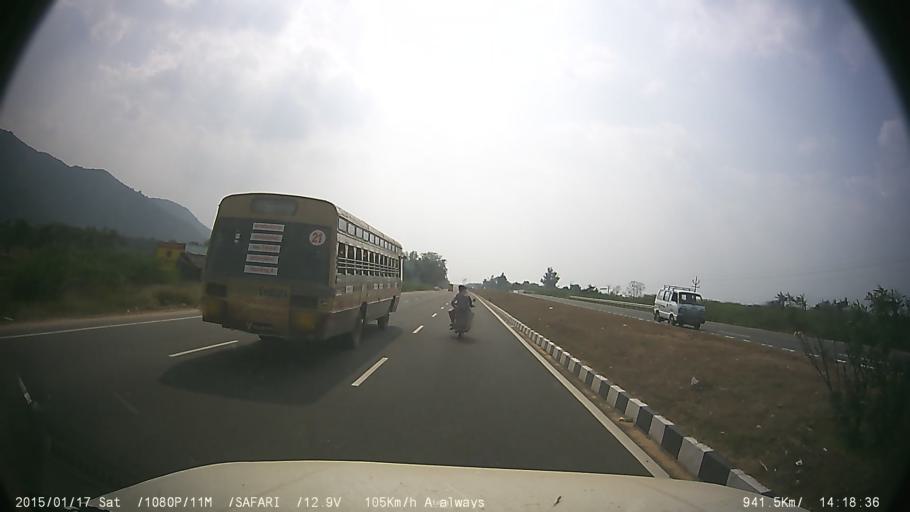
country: IN
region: Tamil Nadu
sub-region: Vellore
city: Vaniyambadi
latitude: 12.7287
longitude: 78.6749
